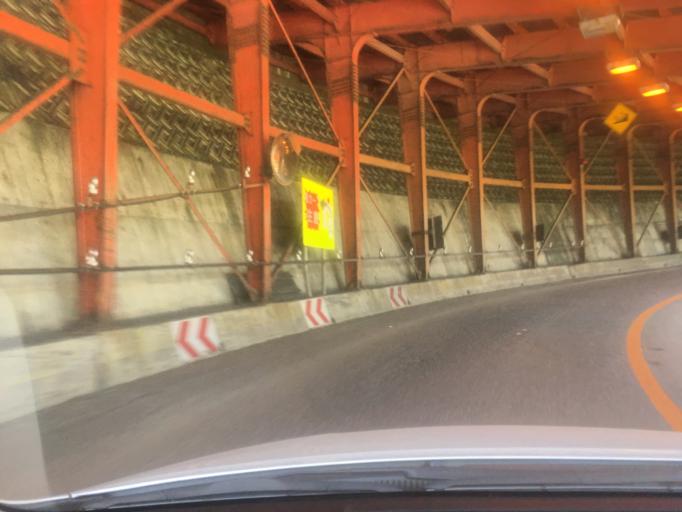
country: JP
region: Niigata
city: Tochio-honcho
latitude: 37.3580
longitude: 139.0536
